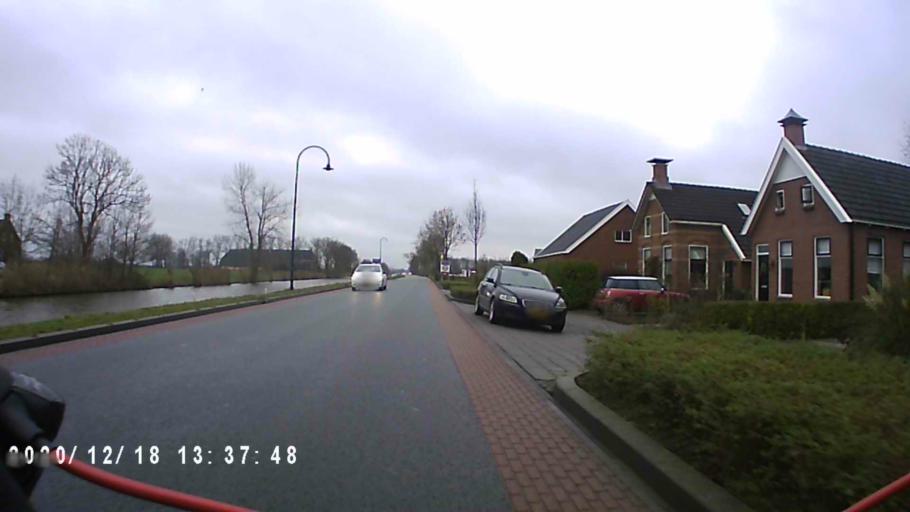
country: NL
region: Groningen
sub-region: Gemeente Bedum
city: Bedum
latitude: 53.3321
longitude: 6.5917
